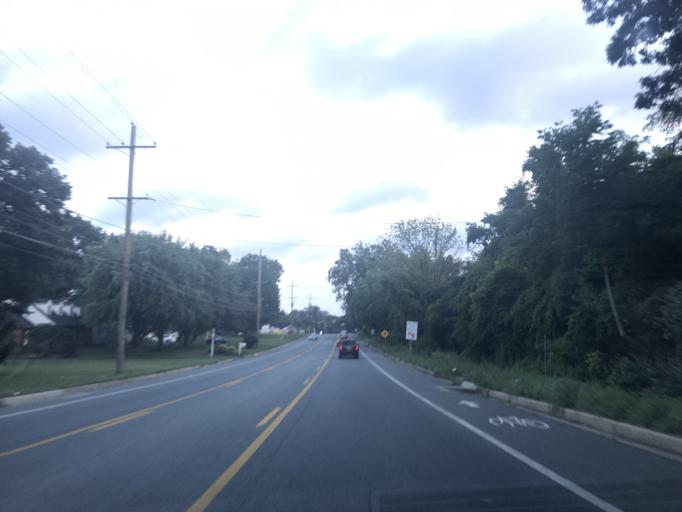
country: US
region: Maryland
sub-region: Cecil County
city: Perryville
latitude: 39.5794
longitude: -76.0671
